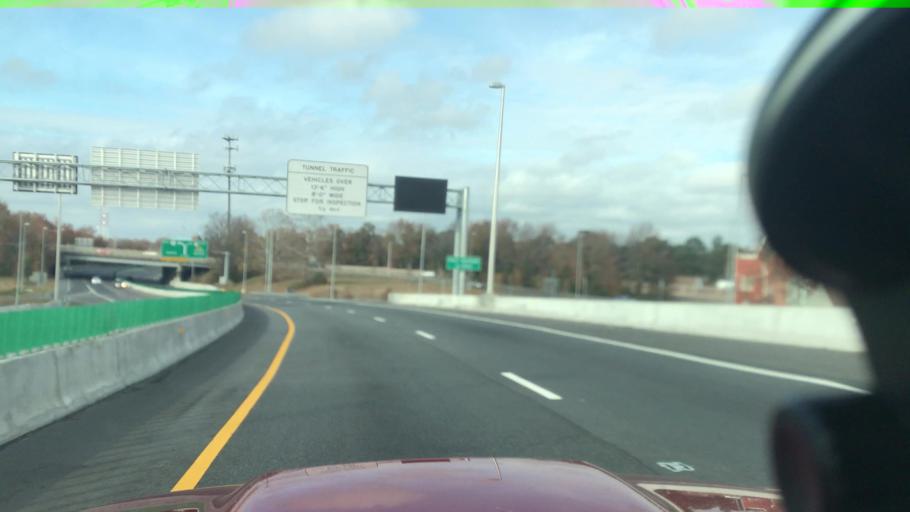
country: US
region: Virginia
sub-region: City of Portsmouth
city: Portsmouth
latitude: 36.8357
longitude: -76.3270
